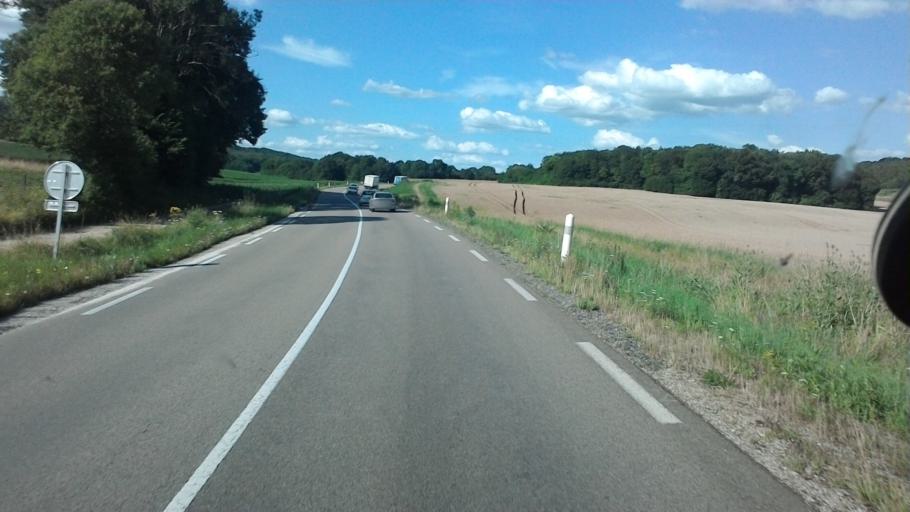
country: FR
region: Franche-Comte
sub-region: Departement de la Haute-Saone
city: Noidans-les-Vesoul
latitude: 47.5923
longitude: 6.1044
